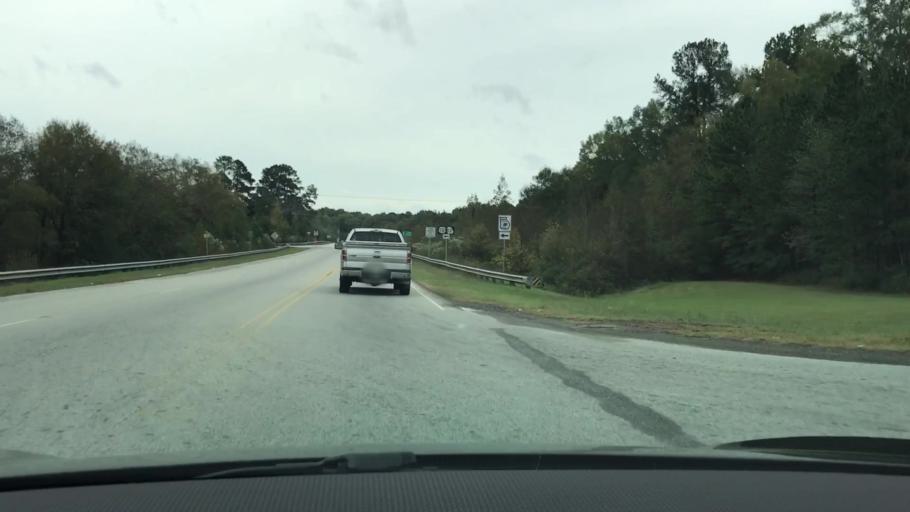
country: US
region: Georgia
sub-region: Warren County
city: West Warrenton
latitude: 33.4080
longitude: -82.6730
